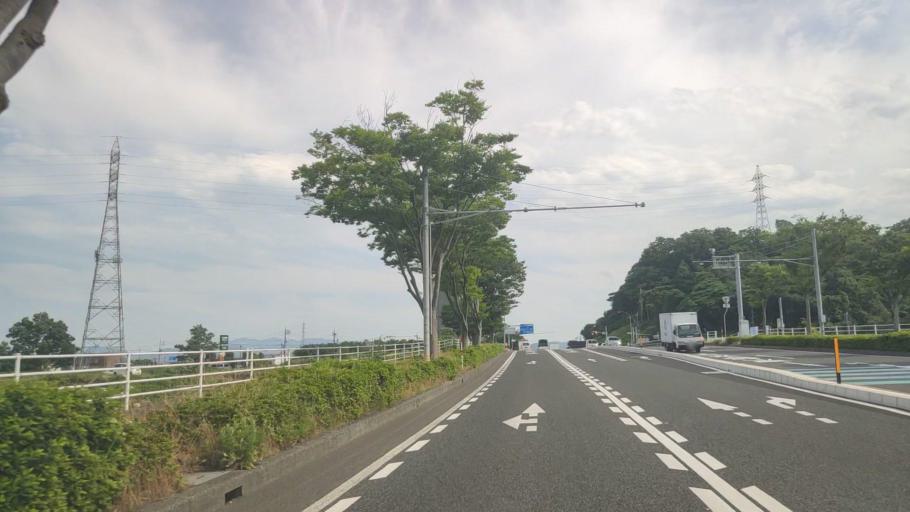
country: JP
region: Tottori
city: Tottori
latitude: 35.5003
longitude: 134.2017
